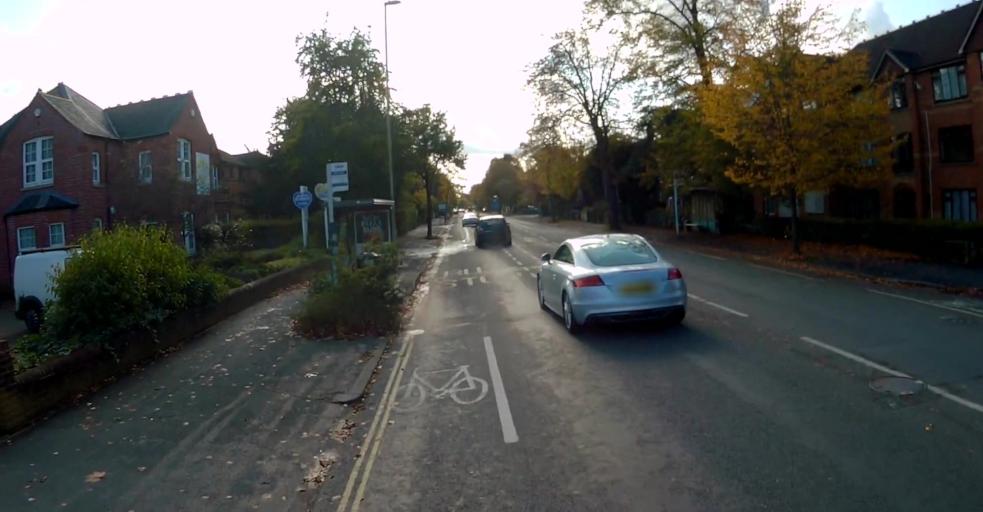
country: GB
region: England
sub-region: Hampshire
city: Farnborough
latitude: 51.2792
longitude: -0.7501
